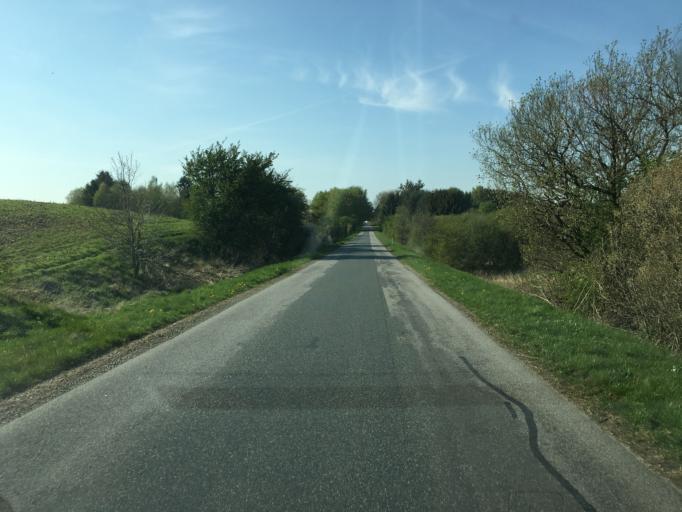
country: DK
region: South Denmark
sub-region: Haderslev Kommune
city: Vojens
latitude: 55.2377
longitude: 9.3252
